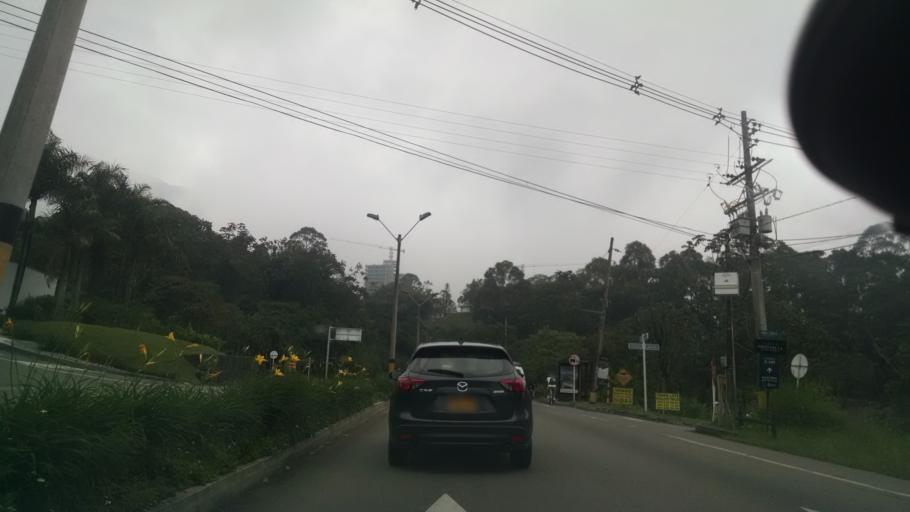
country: CO
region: Antioquia
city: Medellin
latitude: 6.2158
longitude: -75.5524
